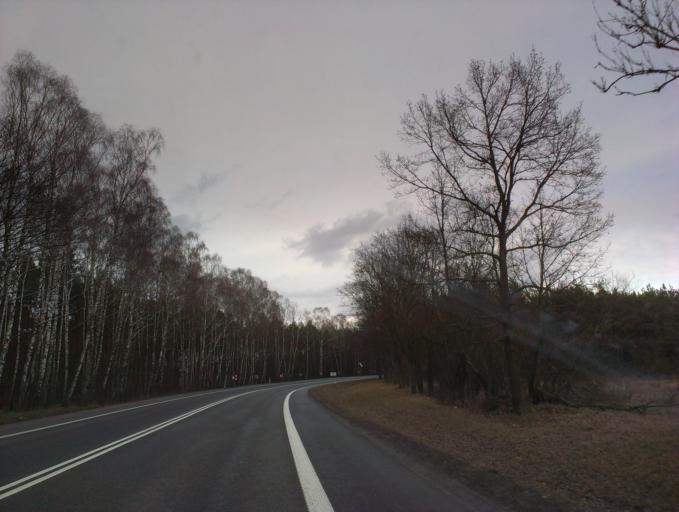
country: PL
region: Masovian Voivodeship
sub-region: Powiat sierpecki
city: Sierpc
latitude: 52.8704
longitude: 19.6377
